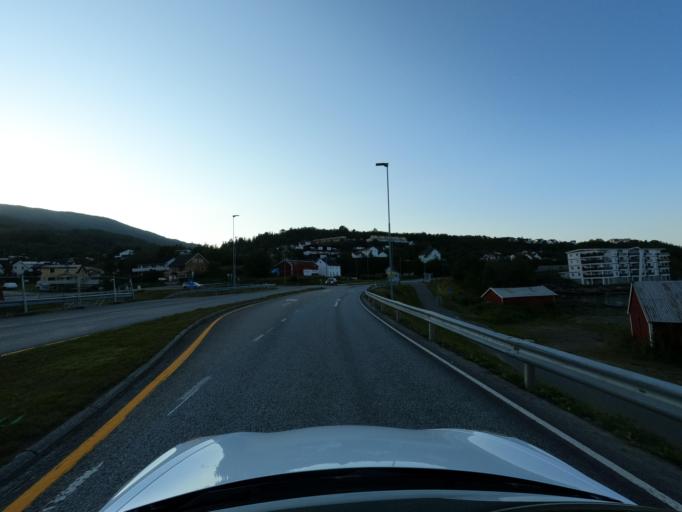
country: NO
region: Troms
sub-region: Harstad
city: Harstad
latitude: 68.7463
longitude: 16.5581
